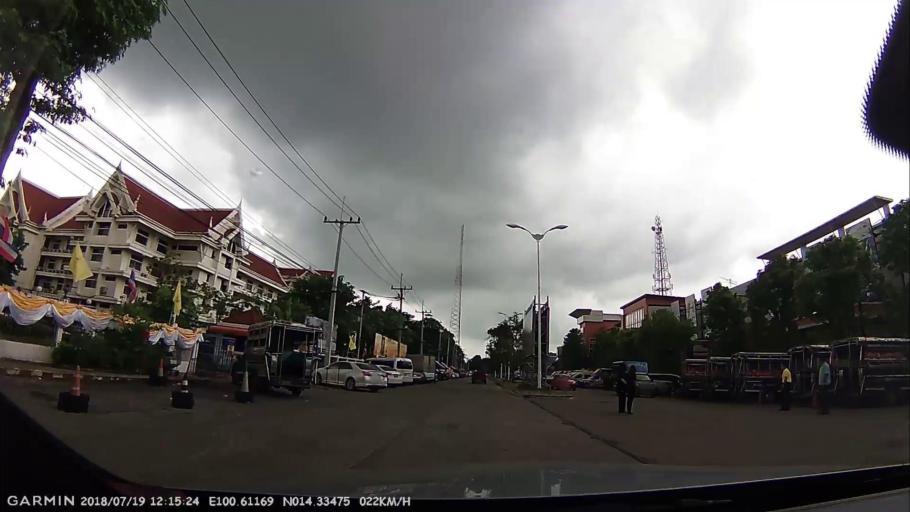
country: TH
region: Phra Nakhon Si Ayutthaya
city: Phra Nakhon Si Ayutthaya
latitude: 14.3348
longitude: 100.6116
